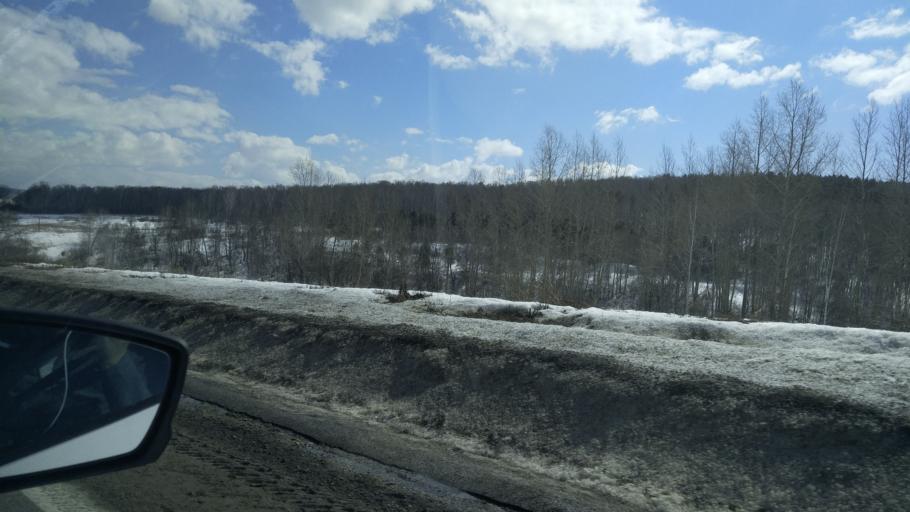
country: RU
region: Kemerovo
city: Yurga
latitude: 55.6724
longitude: 85.1471
